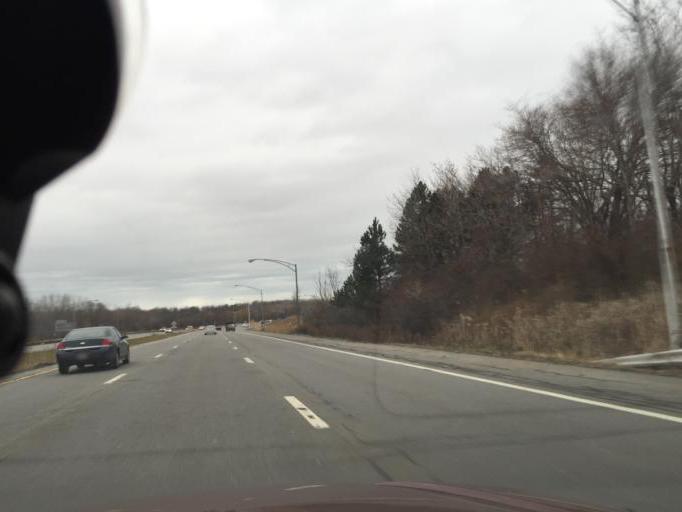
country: US
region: New York
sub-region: Monroe County
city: Greece
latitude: 43.1914
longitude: -77.6828
